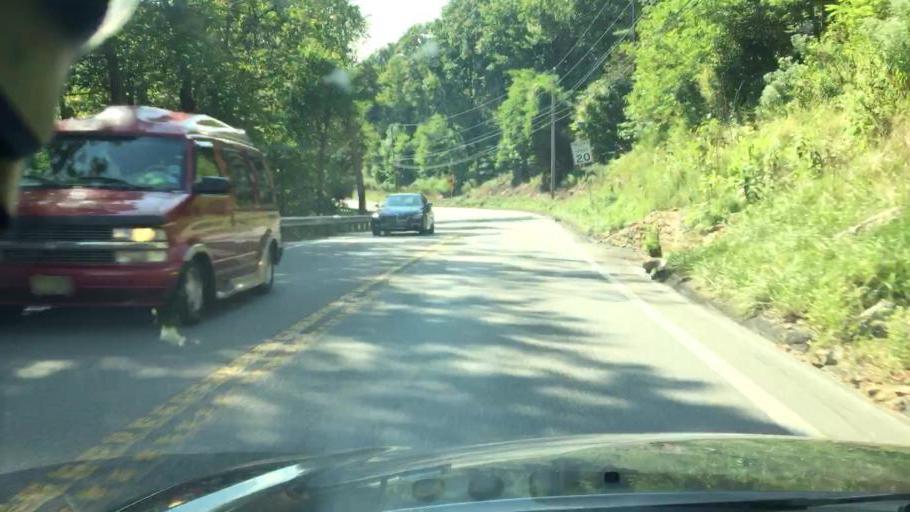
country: US
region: Pennsylvania
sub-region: Carbon County
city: Jim Thorpe
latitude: 40.8879
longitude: -75.7120
